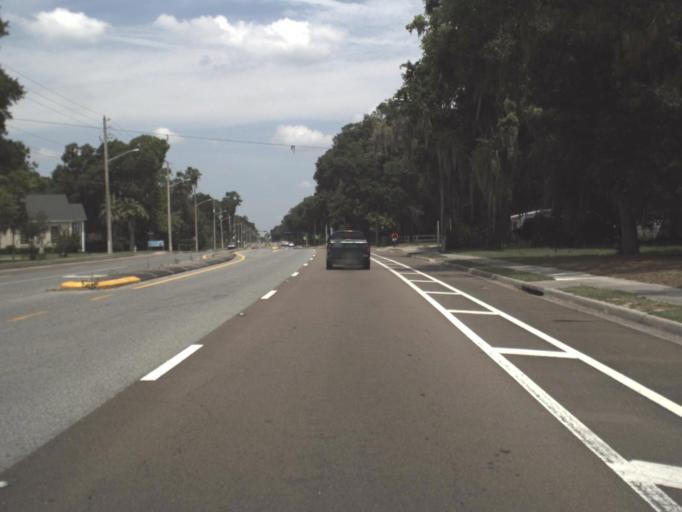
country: US
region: Florida
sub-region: Alachua County
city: Gainesville
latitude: 29.6336
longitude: -82.2686
